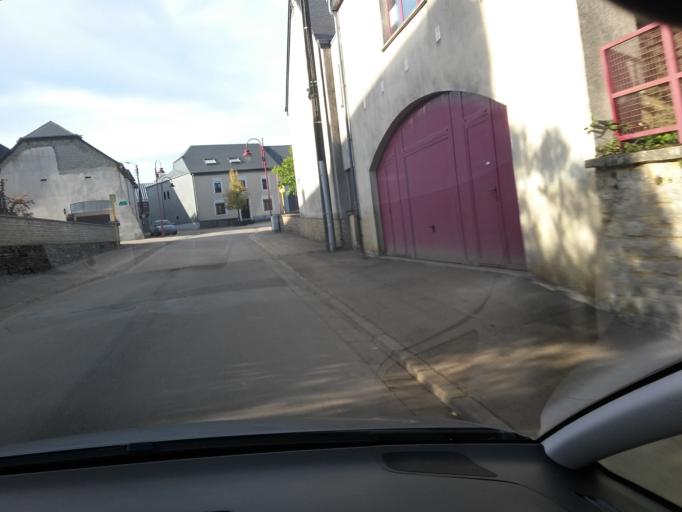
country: BE
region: Wallonia
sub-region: Province du Luxembourg
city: Attert
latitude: 49.7563
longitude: 5.7265
